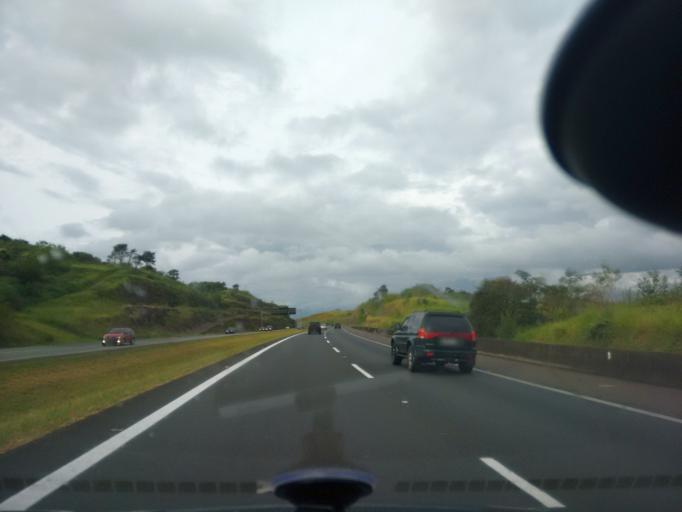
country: BR
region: Sao Paulo
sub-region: Cordeiropolis
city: Cordeiropolis
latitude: -22.5408
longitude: -47.4576
